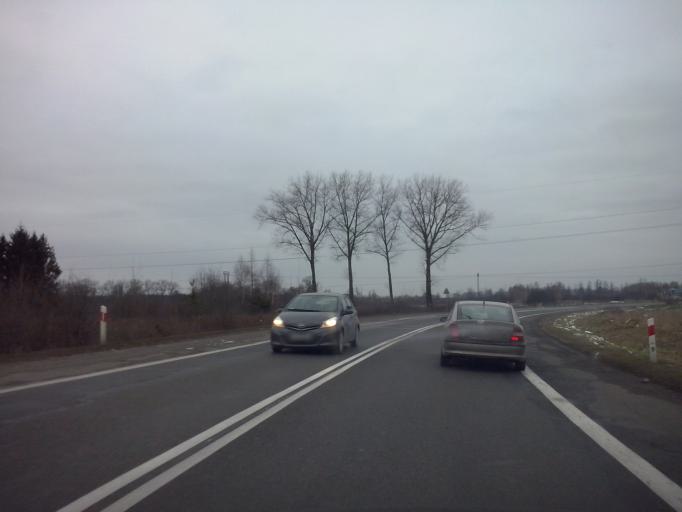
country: PL
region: Subcarpathian Voivodeship
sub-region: Powiat nizanski
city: Zarzecze
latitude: 50.5171
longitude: 22.1847
